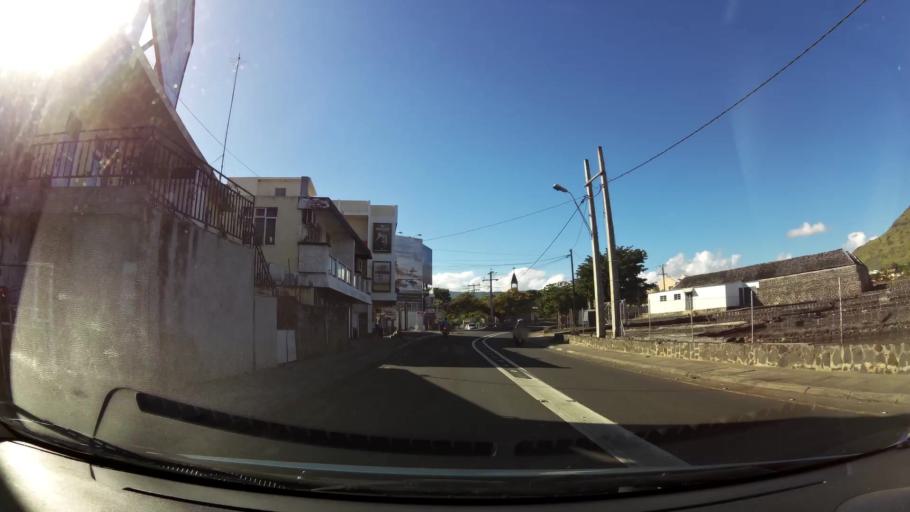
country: MU
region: Black River
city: Tamarin
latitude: -20.3291
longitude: 57.3773
